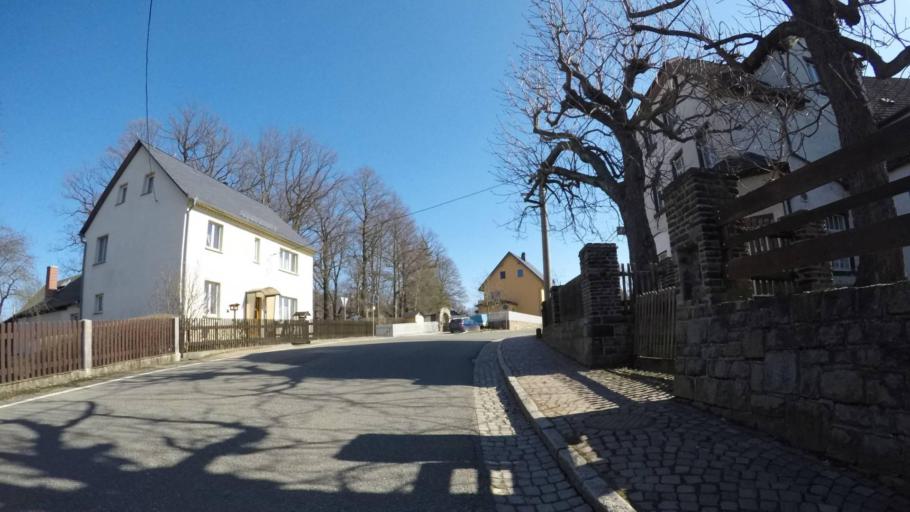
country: DE
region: Saxony
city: Niederfrohna
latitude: 50.9000
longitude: 12.6700
